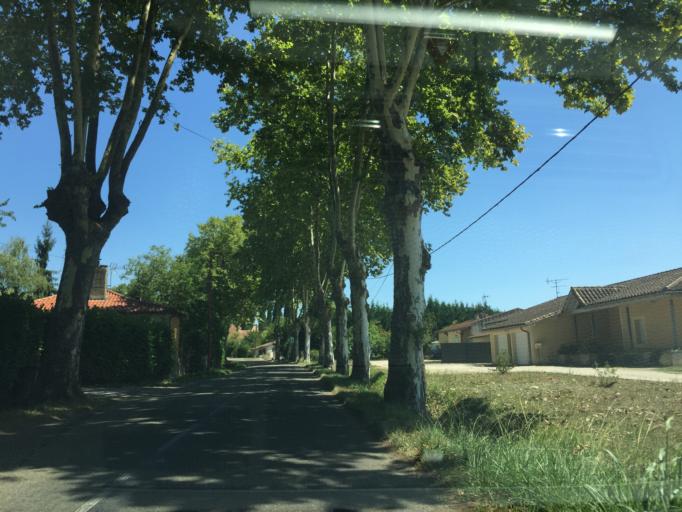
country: FR
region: Midi-Pyrenees
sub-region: Departement du Gers
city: Mirande
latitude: 43.5889
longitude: 0.4147
